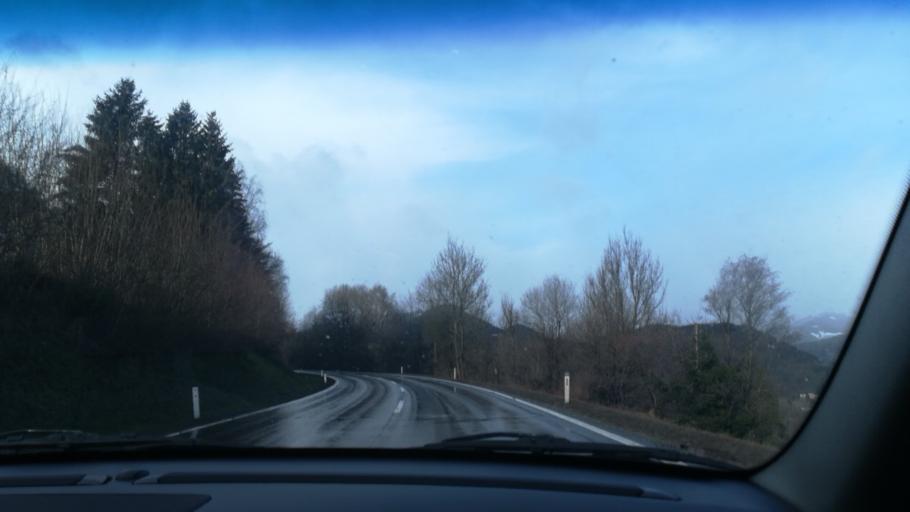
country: AT
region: Styria
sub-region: Politischer Bezirk Murtal
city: Sankt Peter ob Judenburg
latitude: 47.1929
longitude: 14.5820
